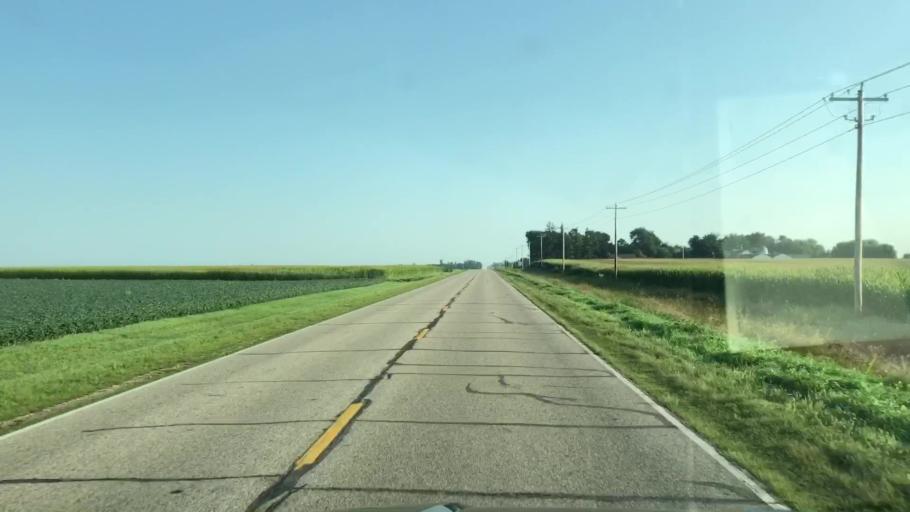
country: US
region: Iowa
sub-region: Lyon County
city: George
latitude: 43.3518
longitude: -95.9983
